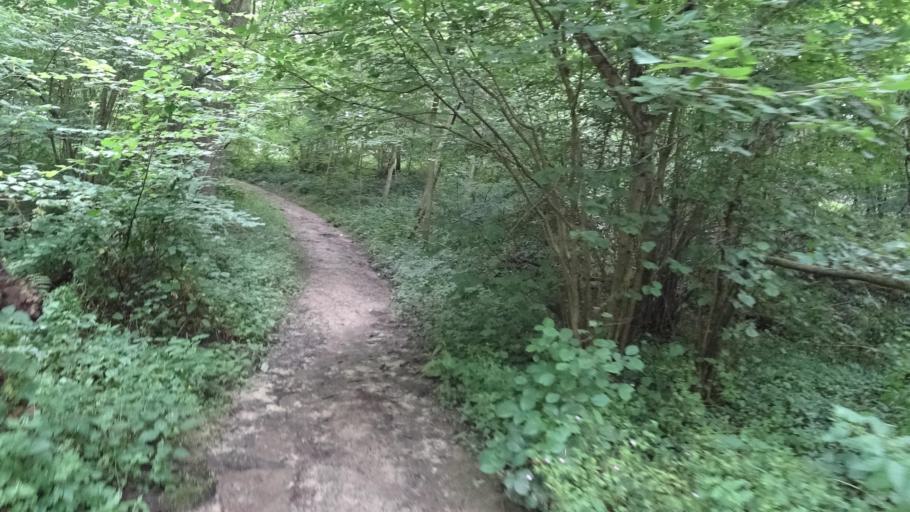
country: BE
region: Wallonia
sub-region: Province du Brabant Wallon
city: Louvain-la-Neuve
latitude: 50.6763
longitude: 4.6068
